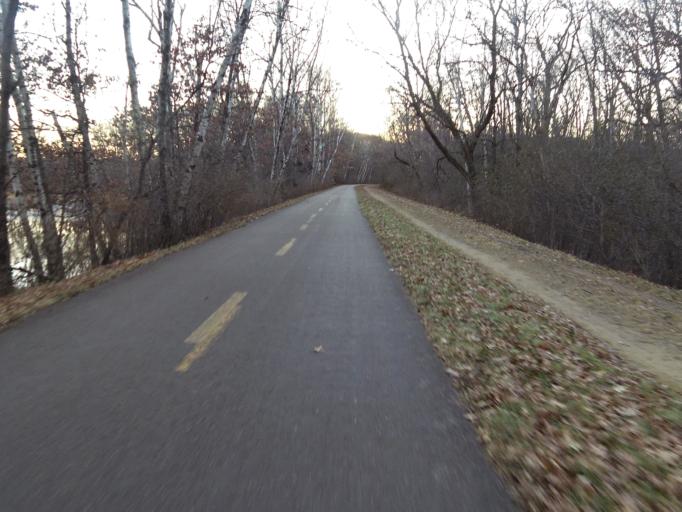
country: US
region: Minnesota
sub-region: Washington County
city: Grant
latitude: 45.0729
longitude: -92.9060
